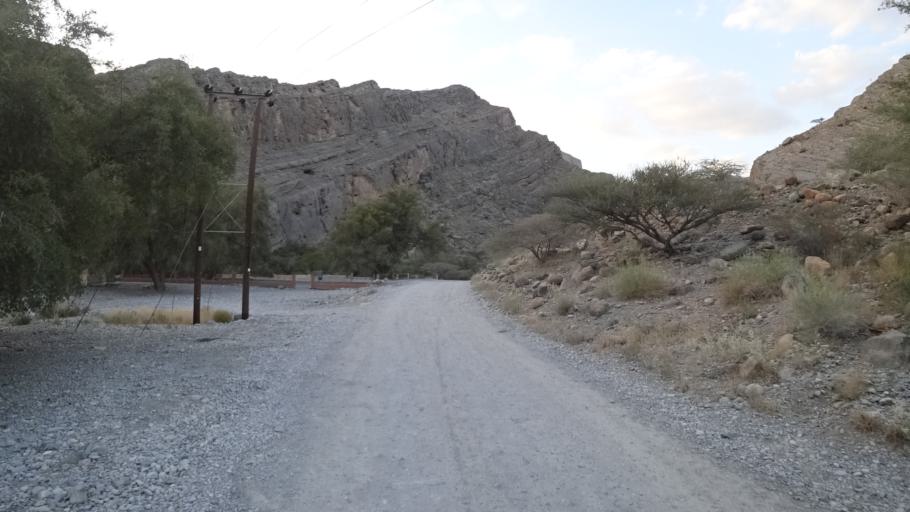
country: OM
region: Muhafazat ad Dakhiliyah
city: Nizwa
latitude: 23.0538
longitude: 57.4685
